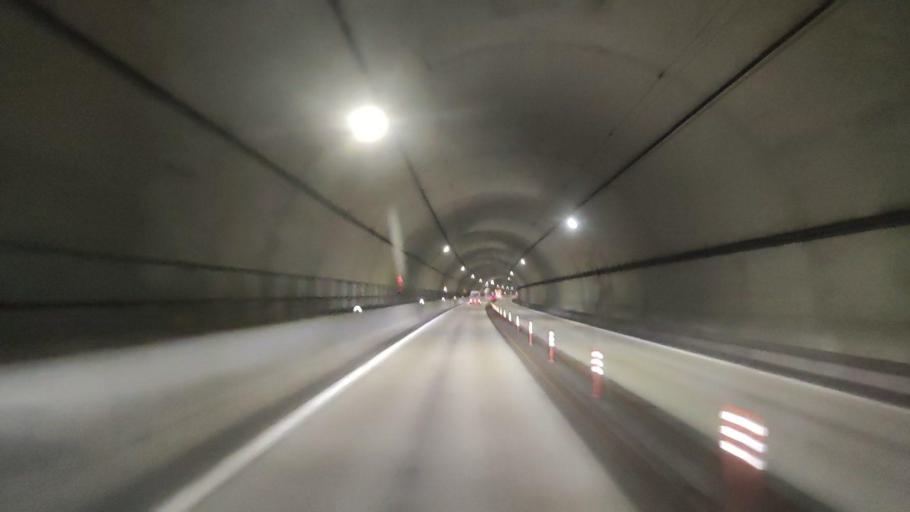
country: JP
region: Wakayama
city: Tanabe
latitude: 33.5918
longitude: 135.4384
